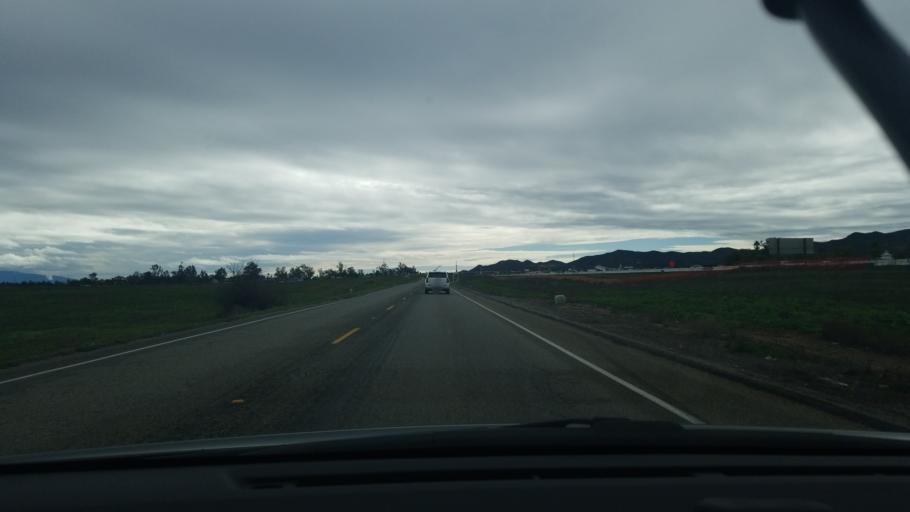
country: US
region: California
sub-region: Riverside County
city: Sun City
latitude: 33.6513
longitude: -117.1704
